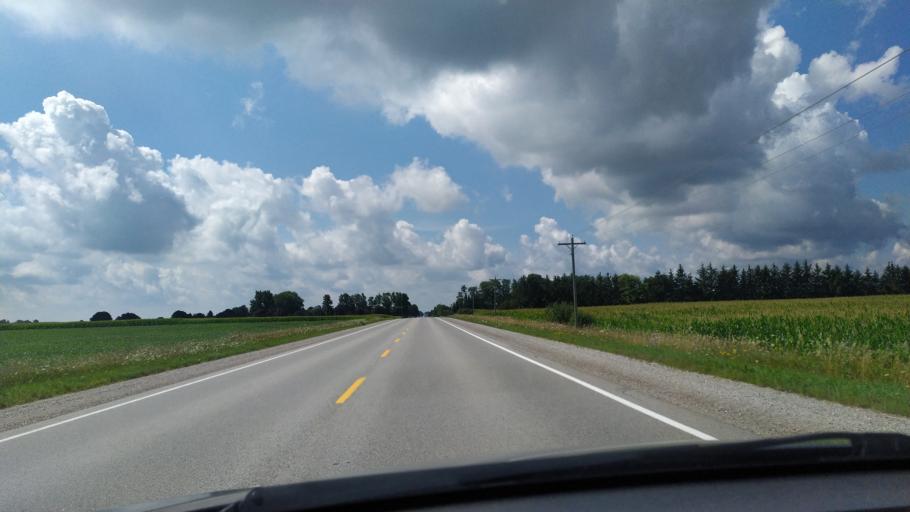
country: CA
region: Ontario
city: South Huron
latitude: 43.3535
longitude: -81.2890
